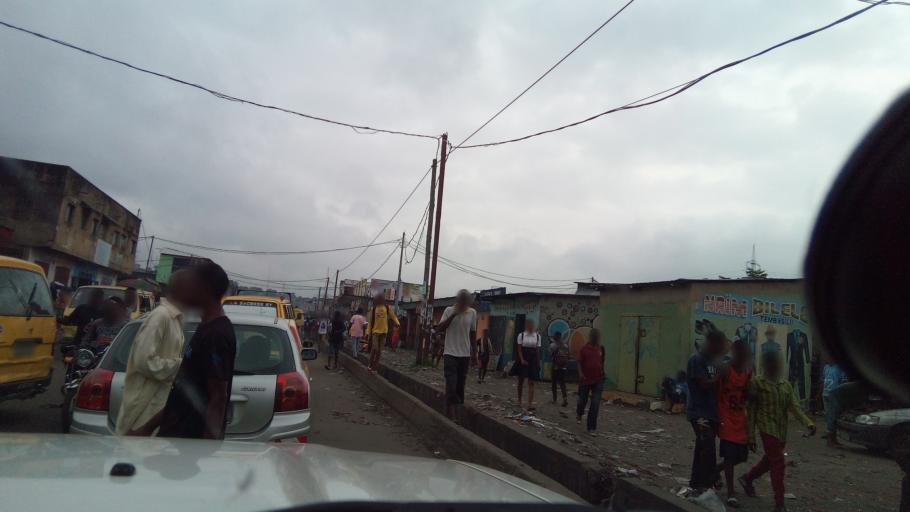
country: CD
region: Kinshasa
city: Kinshasa
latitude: -4.3702
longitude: 15.2846
